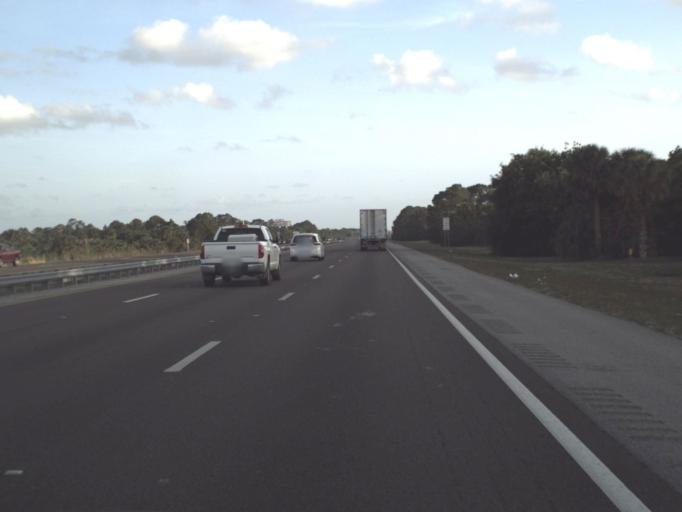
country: US
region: Florida
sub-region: Brevard County
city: Port Saint John
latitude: 28.4431
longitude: -80.8209
